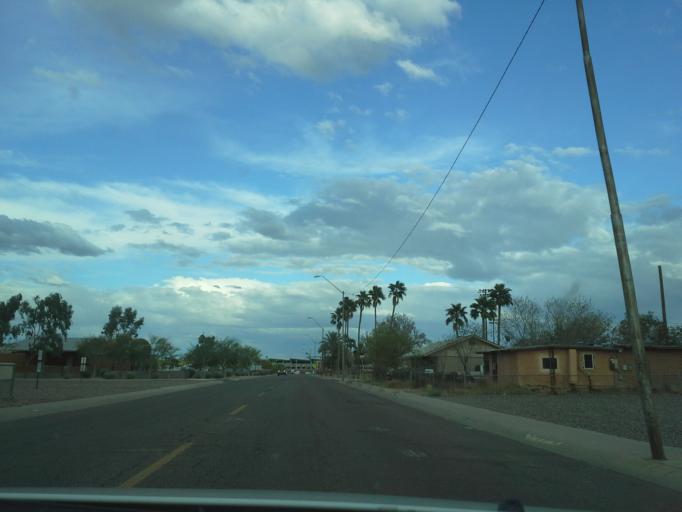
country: US
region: Arizona
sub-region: Maricopa County
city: Phoenix
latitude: 33.4314
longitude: -112.0533
